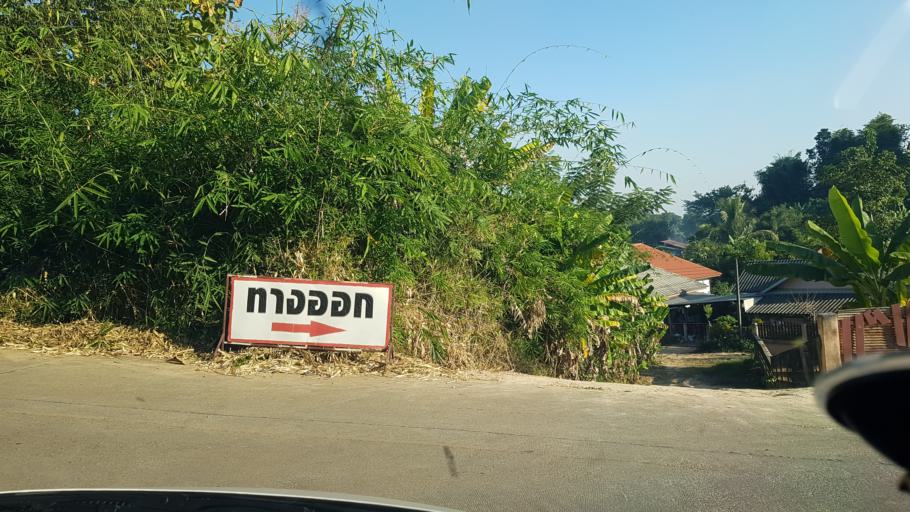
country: TH
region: Chiang Rai
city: Chiang Rai
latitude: 19.9482
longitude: 99.8076
